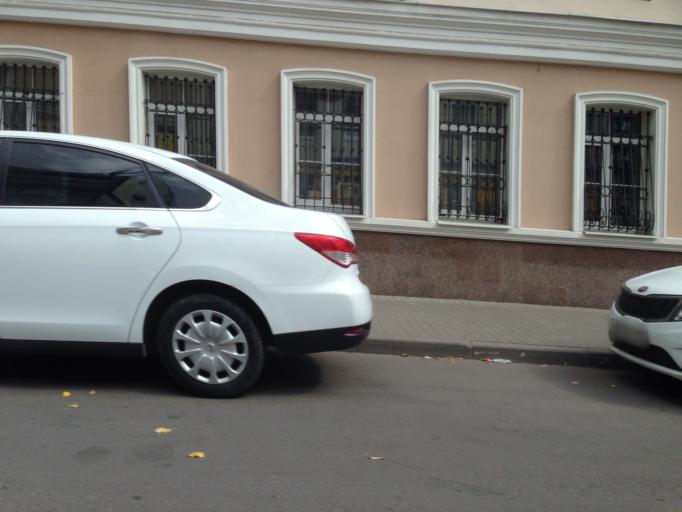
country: RU
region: Voronezj
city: Voronezh
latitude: 51.6654
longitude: 39.1996
